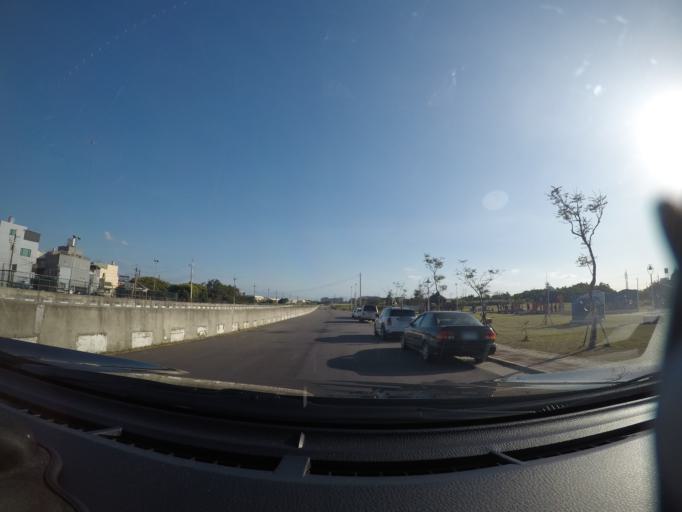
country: TW
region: Taiwan
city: Taoyuan City
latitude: 25.1081
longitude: 121.2537
